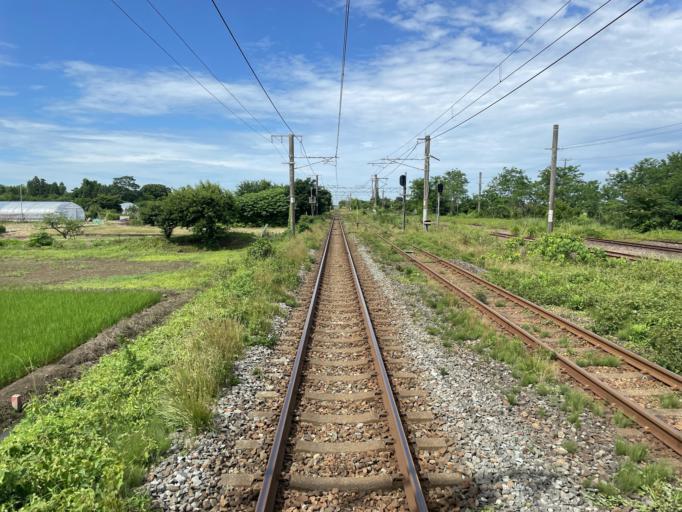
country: JP
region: Niigata
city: Suibara
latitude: 37.9353
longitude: 139.2382
